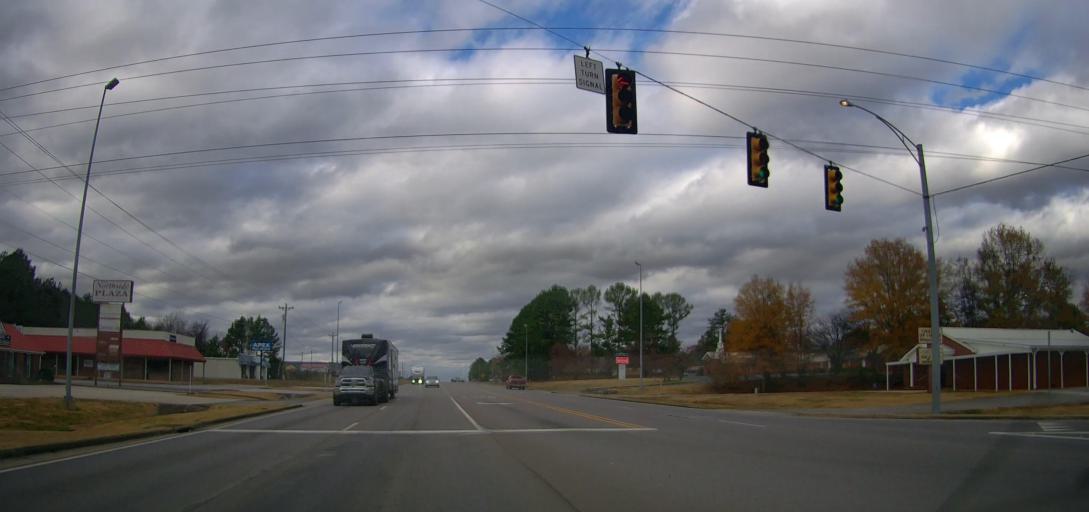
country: US
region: Alabama
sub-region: Lawrence County
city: Moulton
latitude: 34.4953
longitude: -87.2806
